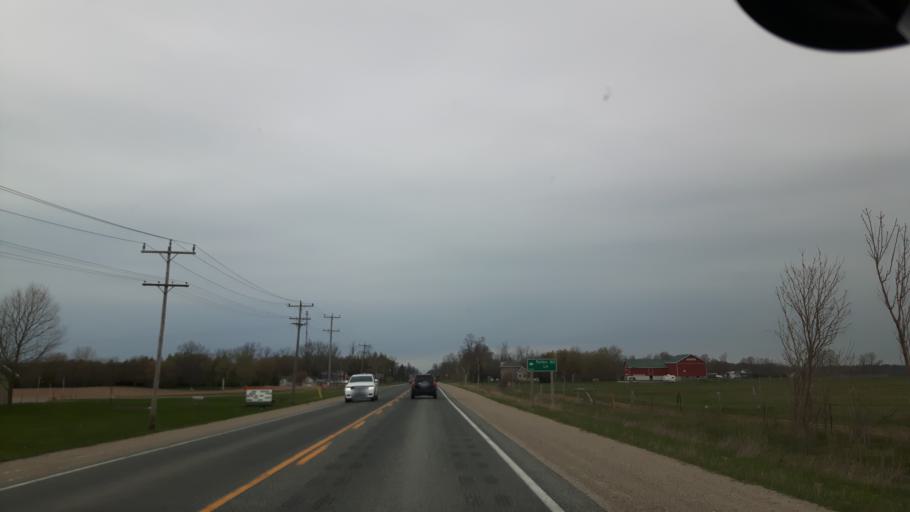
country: CA
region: Ontario
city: Goderich
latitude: 43.7107
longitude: -81.6606
